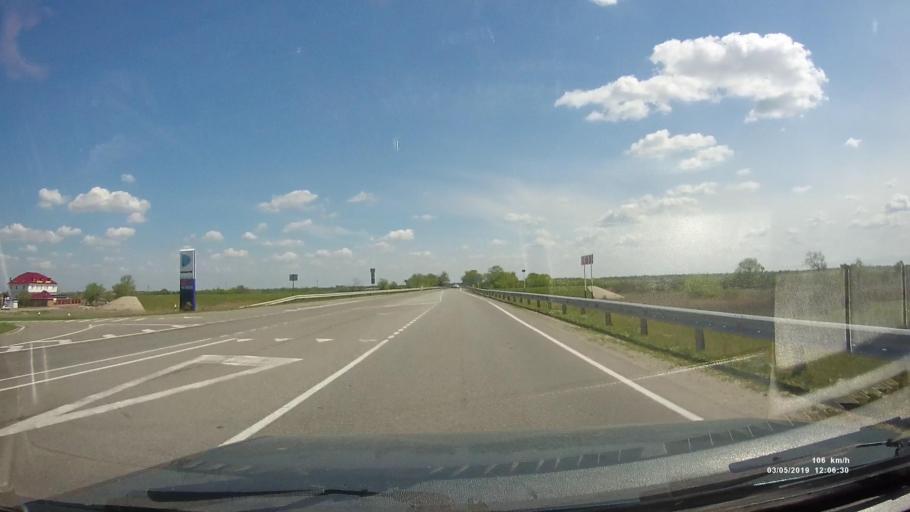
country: RU
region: Rostov
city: Bagayevskaya
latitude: 47.2855
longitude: 40.4534
